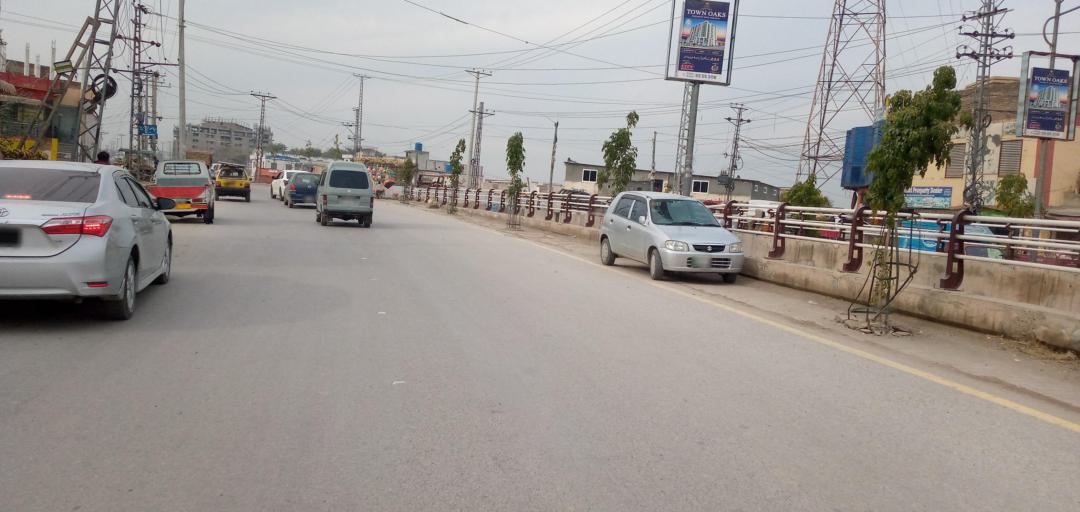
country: PK
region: Khyber Pakhtunkhwa
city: Peshawar
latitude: 34.0025
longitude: 71.4679
